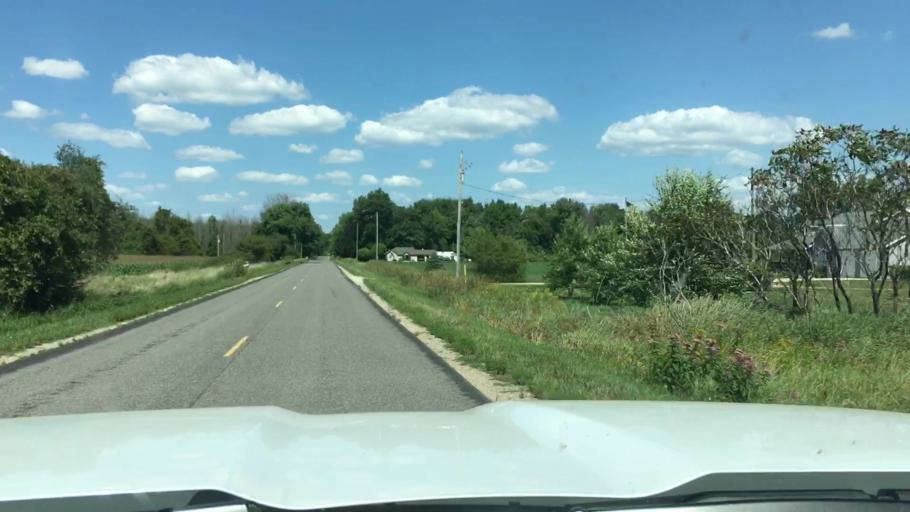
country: US
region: Michigan
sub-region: Muskegon County
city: Ravenna
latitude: 43.2721
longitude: -85.9181
